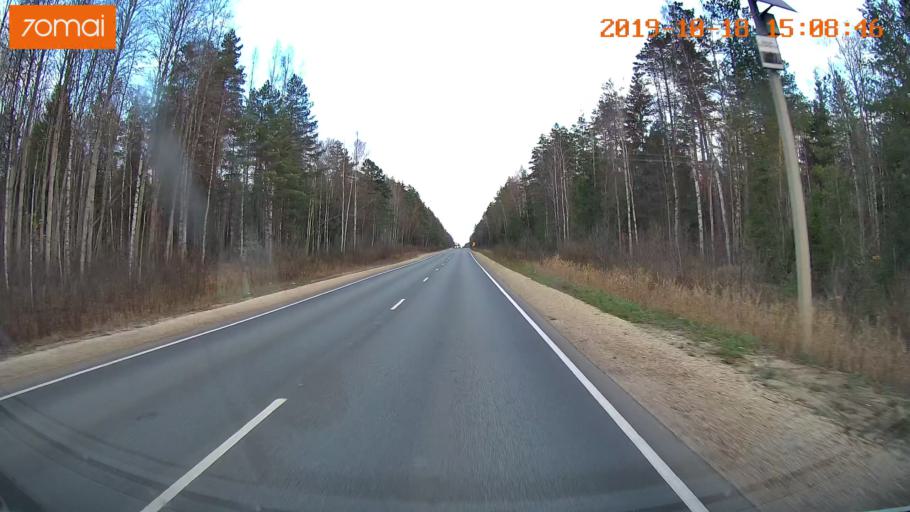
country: RU
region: Vladimir
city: Gus'-Khrustal'nyy
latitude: 55.5567
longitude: 40.6139
